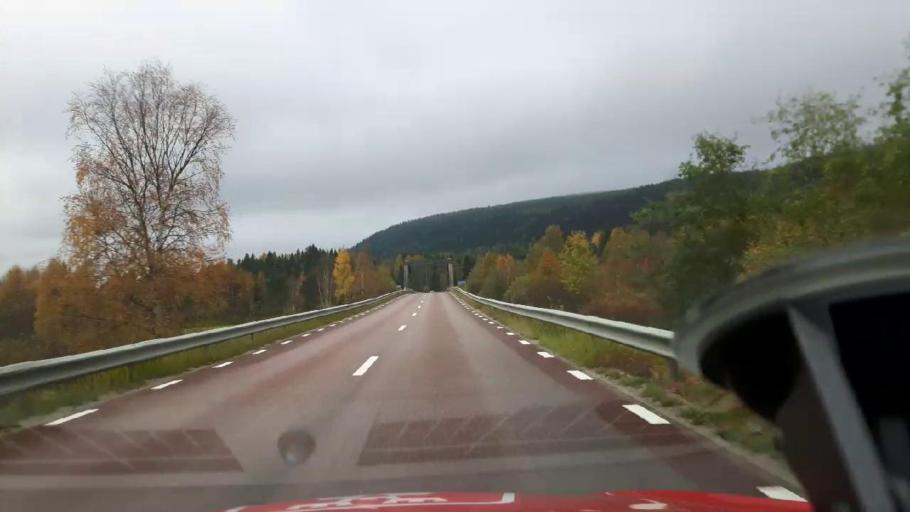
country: SE
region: Jaemtland
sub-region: Harjedalens Kommun
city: Sveg
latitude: 62.2756
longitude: 14.8056
